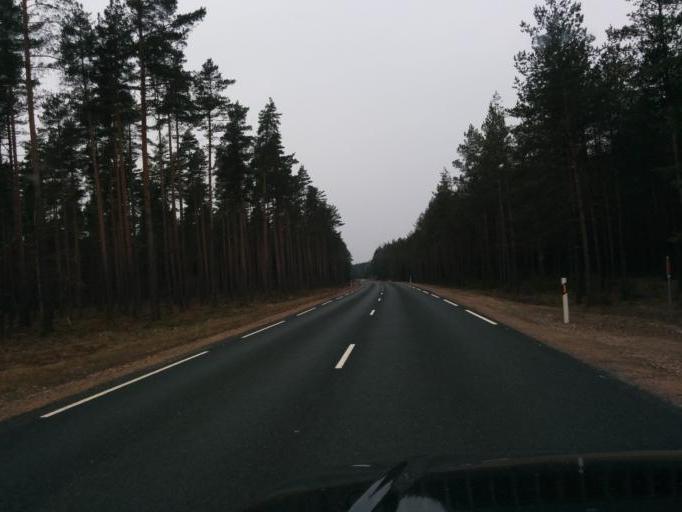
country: LV
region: Ogre
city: Ogre
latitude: 56.8004
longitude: 24.5867
